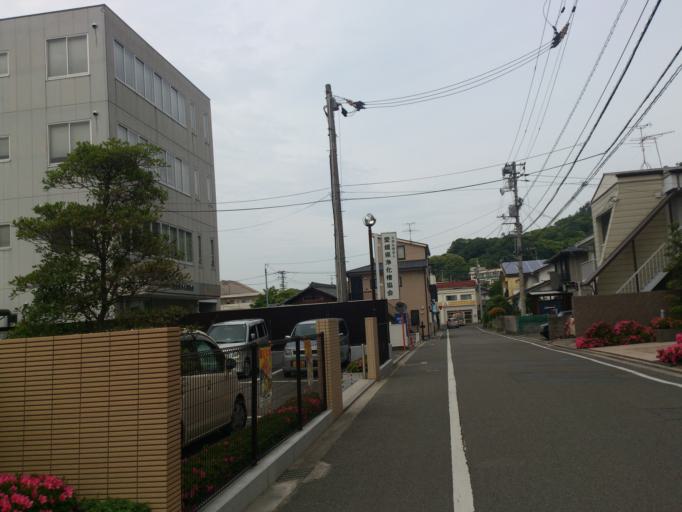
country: JP
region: Ehime
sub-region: Shikoku-chuo Shi
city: Matsuyama
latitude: 33.8418
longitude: 132.7479
